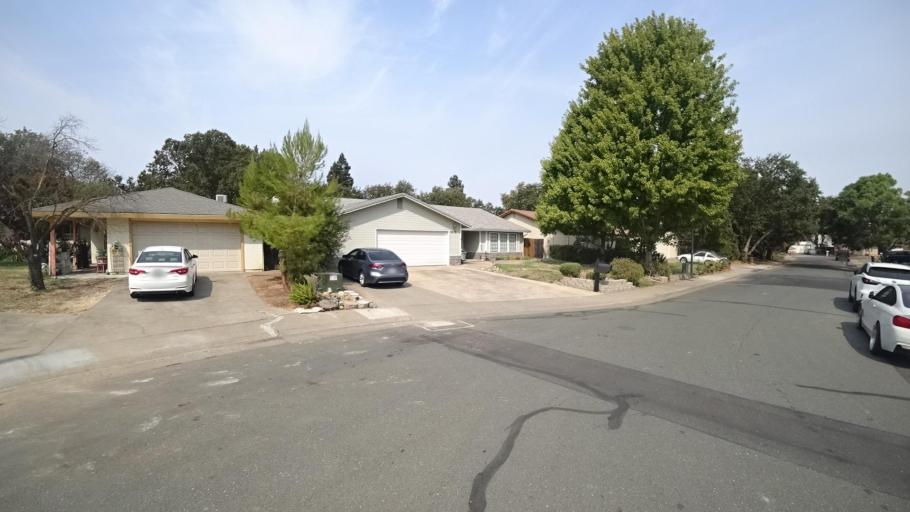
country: US
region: California
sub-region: Sacramento County
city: Elk Grove
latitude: 38.4037
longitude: -121.3736
